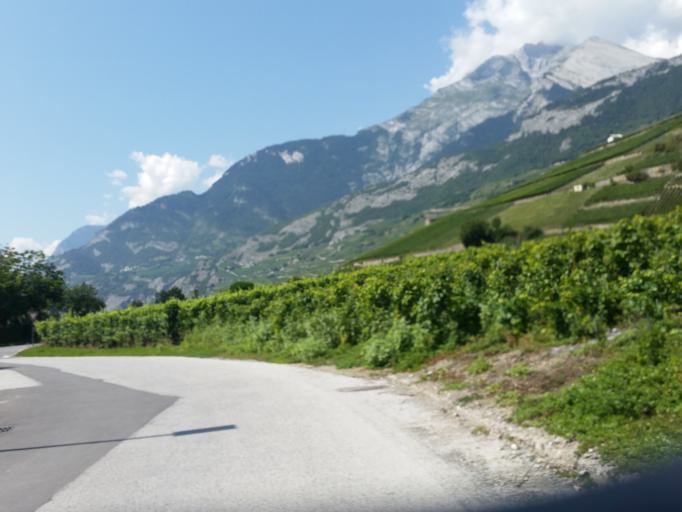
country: CH
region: Valais
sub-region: Conthey District
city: Vetroz
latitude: 46.2288
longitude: 7.2958
